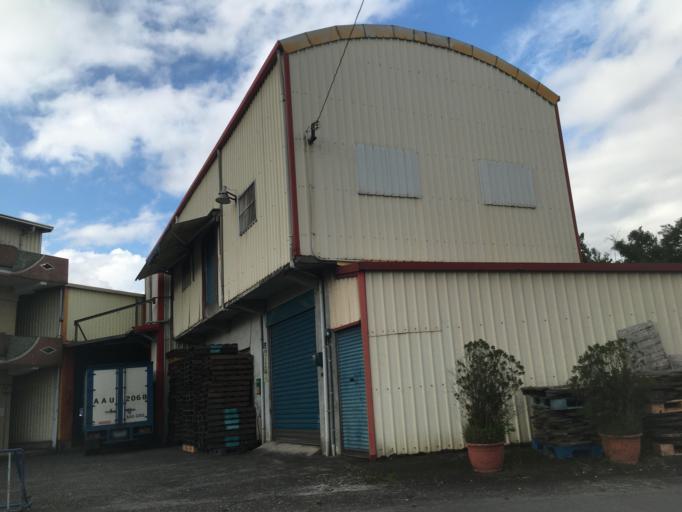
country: TW
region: Taiwan
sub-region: Yilan
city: Yilan
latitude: 24.6913
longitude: 121.7274
